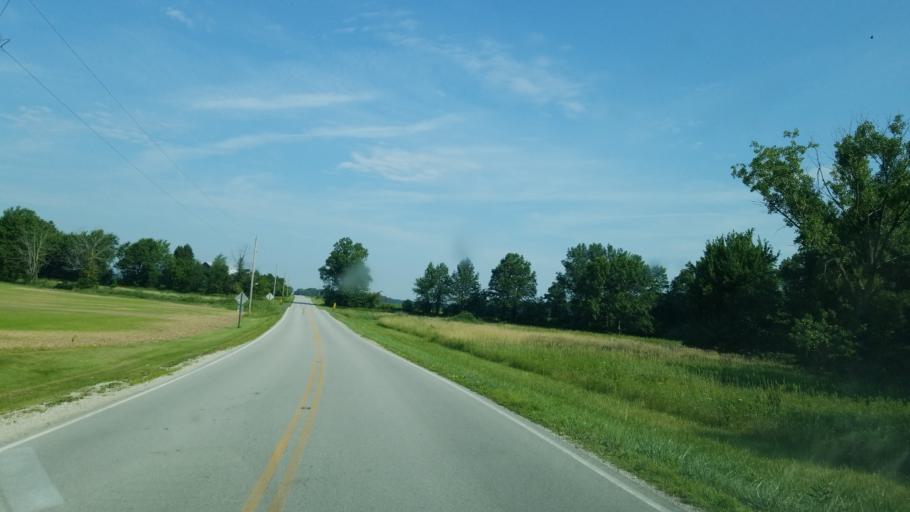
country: US
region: Ohio
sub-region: Huron County
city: Willard
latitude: 41.0100
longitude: -82.8529
